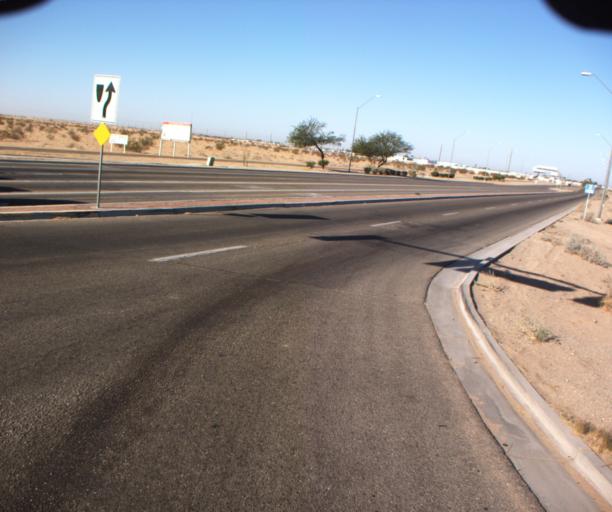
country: US
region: Arizona
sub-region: Yuma County
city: Fortuna Foothills
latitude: 32.6705
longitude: -114.4958
